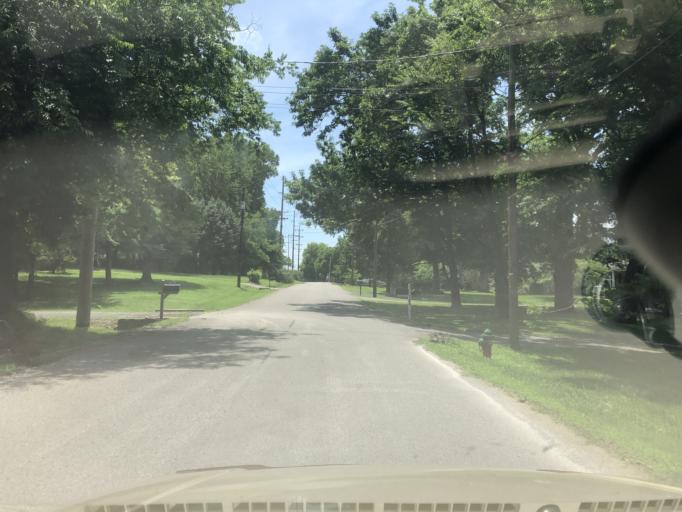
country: US
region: Tennessee
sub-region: Davidson County
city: Lakewood
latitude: 36.2491
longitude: -86.6996
